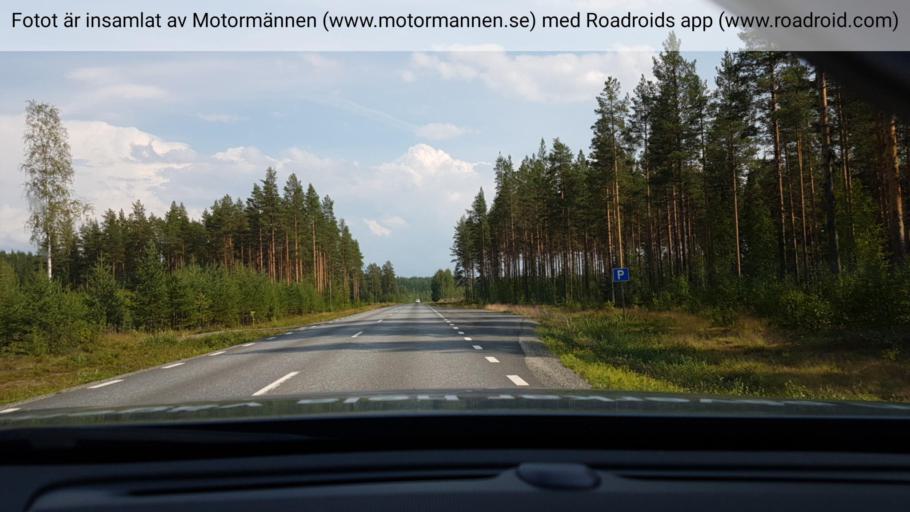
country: SE
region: Vaesterbotten
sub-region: Bjurholms Kommun
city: Bjurholm
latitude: 64.3837
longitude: 19.1173
